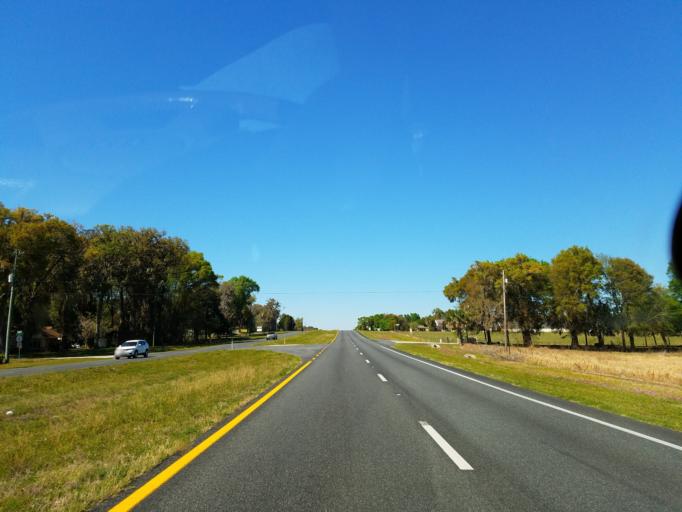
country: US
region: Florida
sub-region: Marion County
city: Belleview
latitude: 29.0395
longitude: -82.0450
